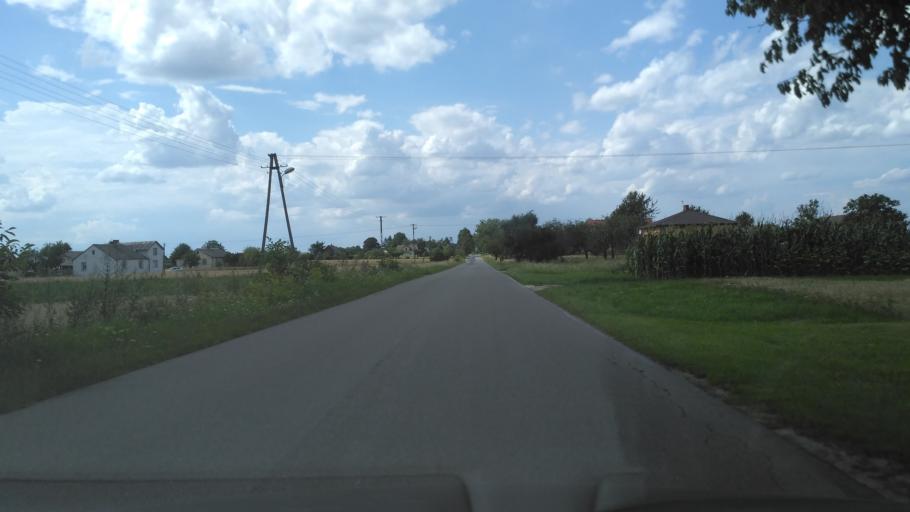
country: PL
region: Lublin Voivodeship
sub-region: Powiat swidnicki
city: Trawniki
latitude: 51.1813
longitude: 22.9582
